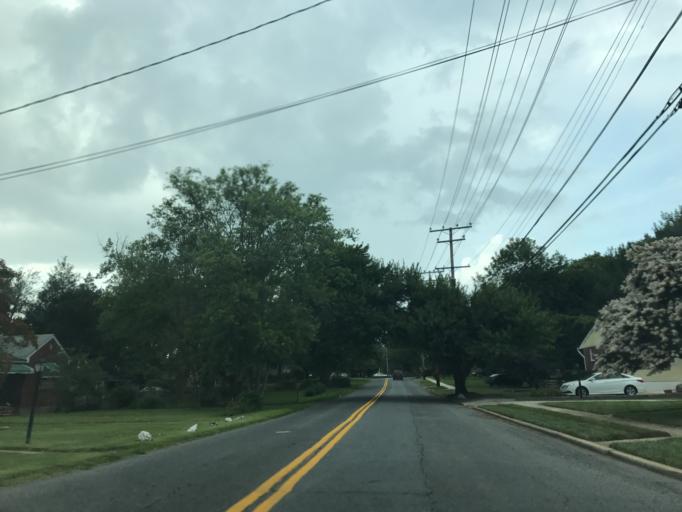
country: US
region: Maryland
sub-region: Baltimore County
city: Lochearn
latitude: 39.3473
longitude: -76.7229
